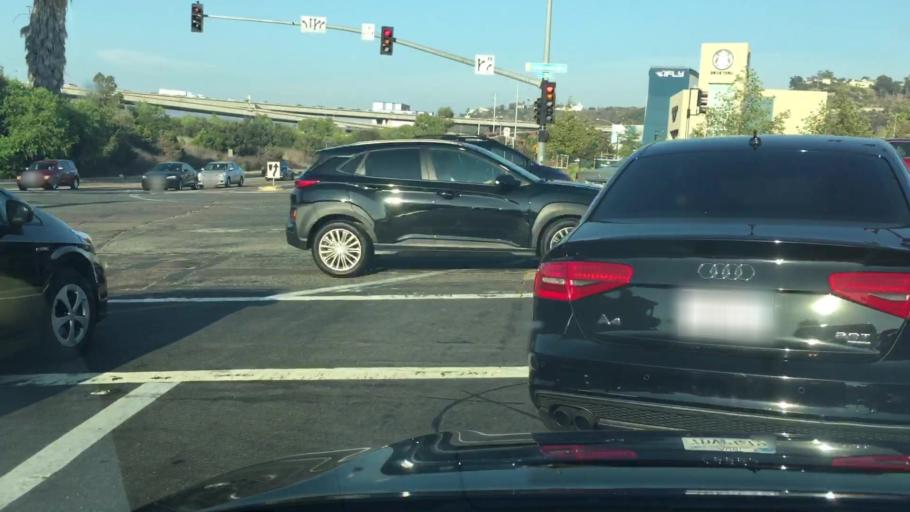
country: US
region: California
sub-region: San Diego County
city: San Diego
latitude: 32.7718
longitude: -117.1404
